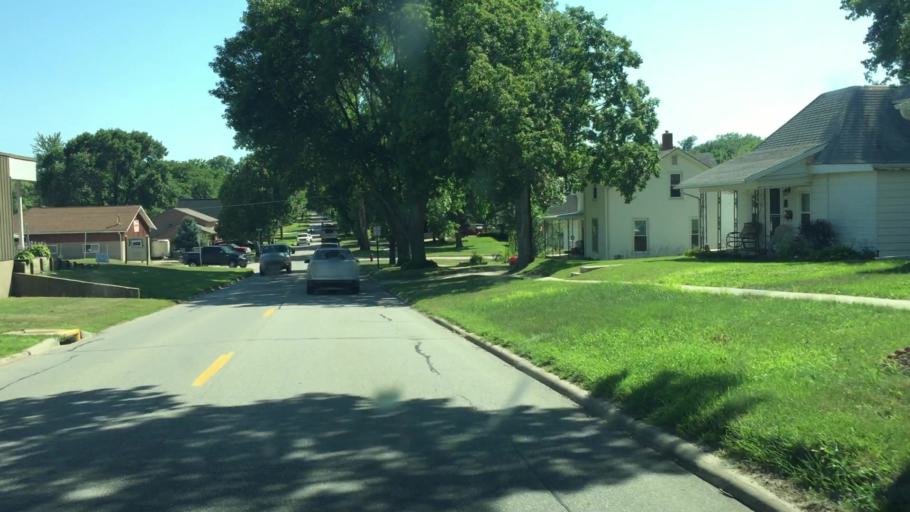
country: US
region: Iowa
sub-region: Linn County
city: Mount Vernon
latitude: 41.9267
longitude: -91.4127
